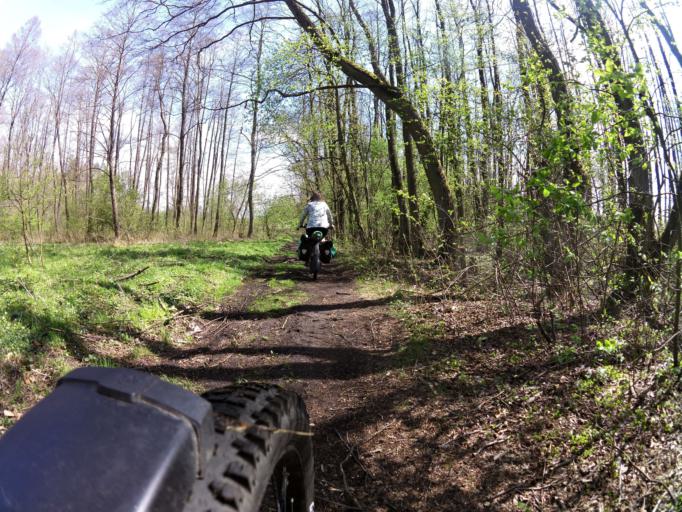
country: PL
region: West Pomeranian Voivodeship
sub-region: Powiat lobeski
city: Resko
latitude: 53.8081
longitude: 15.4535
